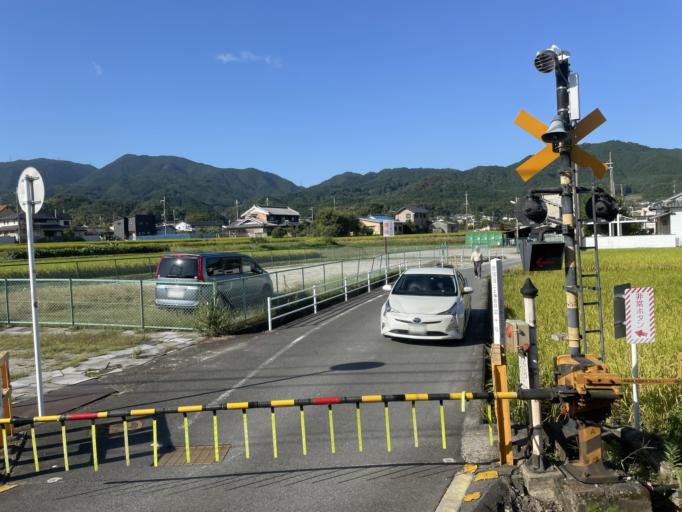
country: JP
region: Nara
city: Gose
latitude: 34.5184
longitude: 135.7044
